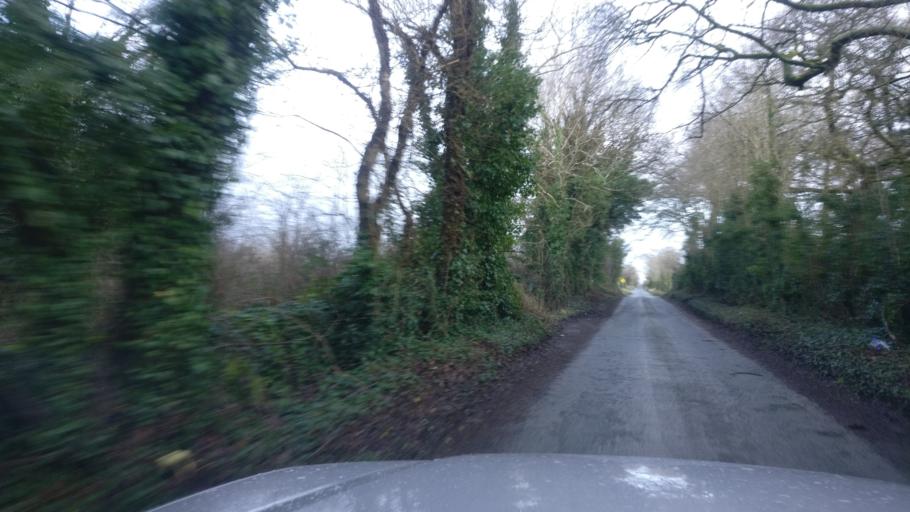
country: IE
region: Connaught
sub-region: County Galway
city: Athenry
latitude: 53.2629
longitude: -8.7014
